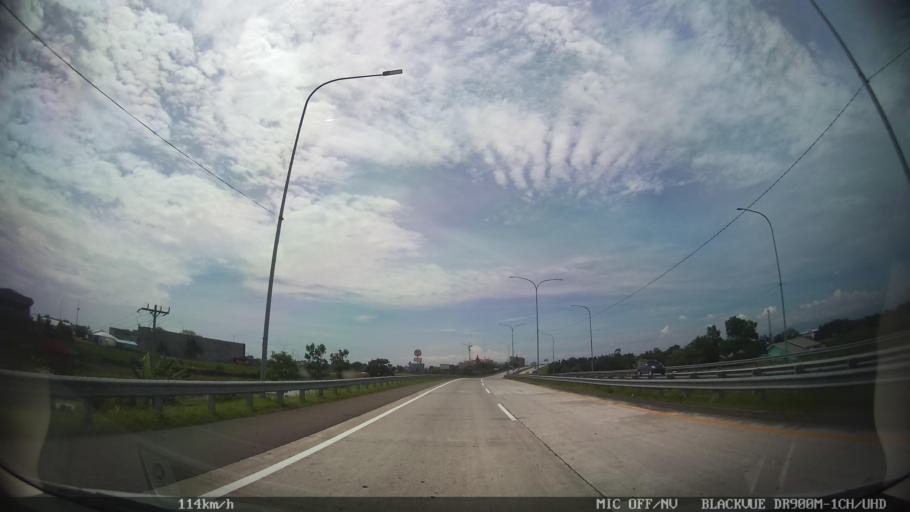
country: ID
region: North Sumatra
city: Percut
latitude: 3.5596
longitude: 98.8516
